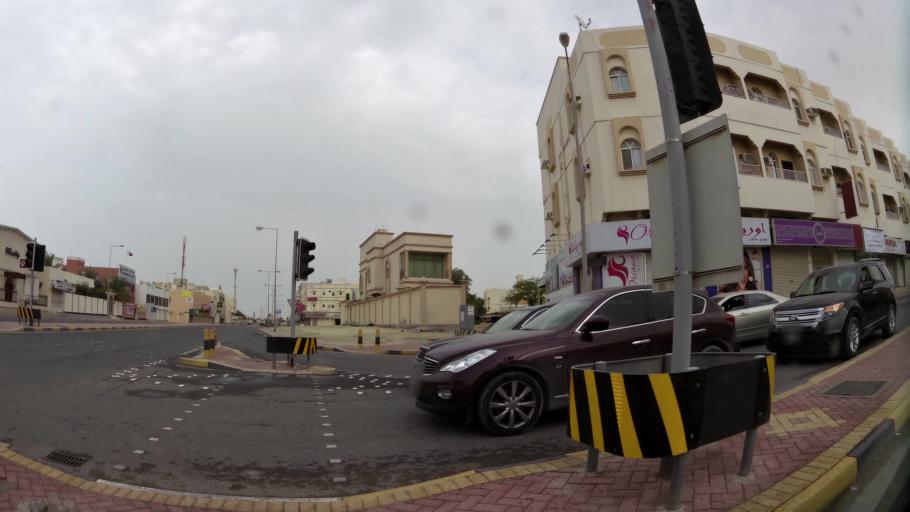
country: BH
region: Northern
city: Ar Rifa'
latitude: 26.1350
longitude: 50.5538
